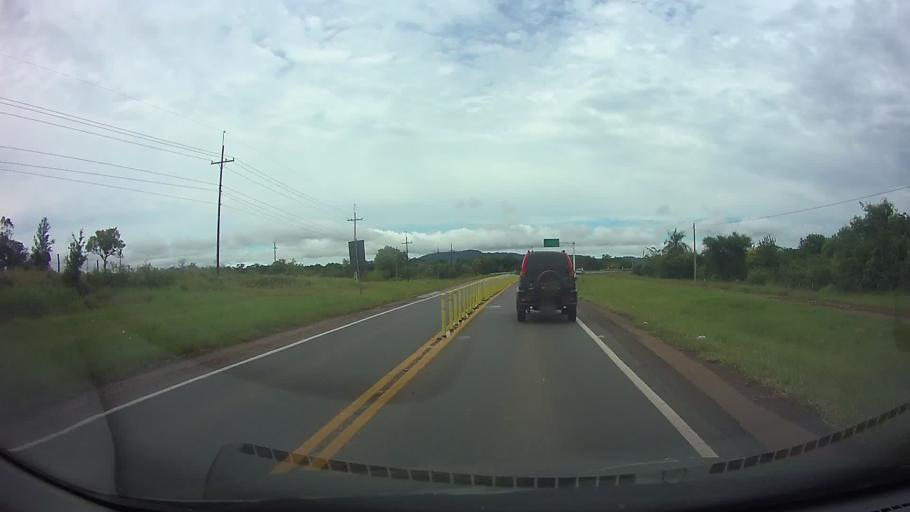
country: PY
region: Paraguari
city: Carapegua
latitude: -25.7461
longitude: -57.2141
